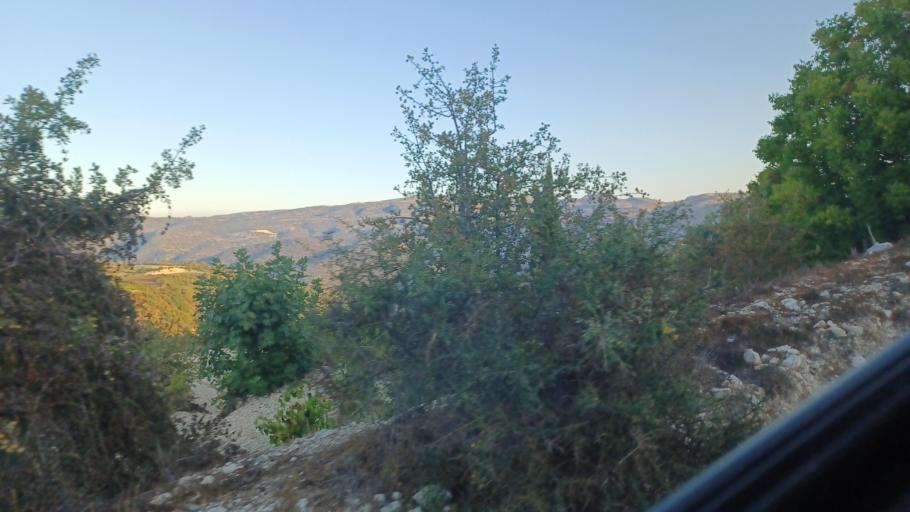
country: CY
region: Pafos
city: Tala
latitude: 34.8650
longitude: 32.4648
